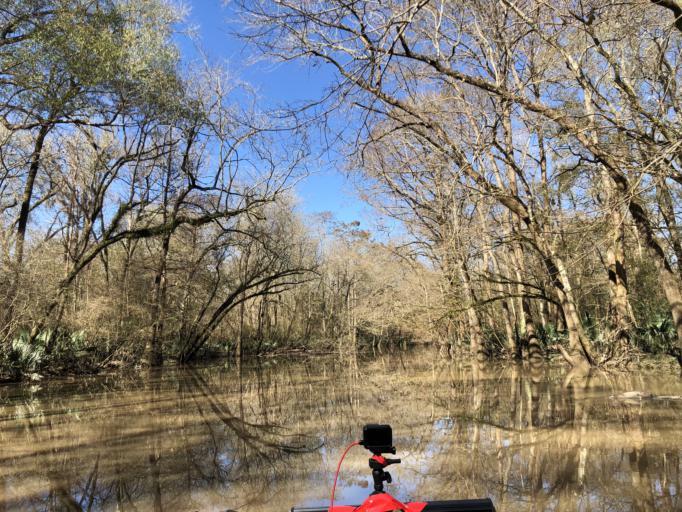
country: US
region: Louisiana
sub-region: Calcasieu Parish
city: Iowa
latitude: 30.3163
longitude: -93.0776
